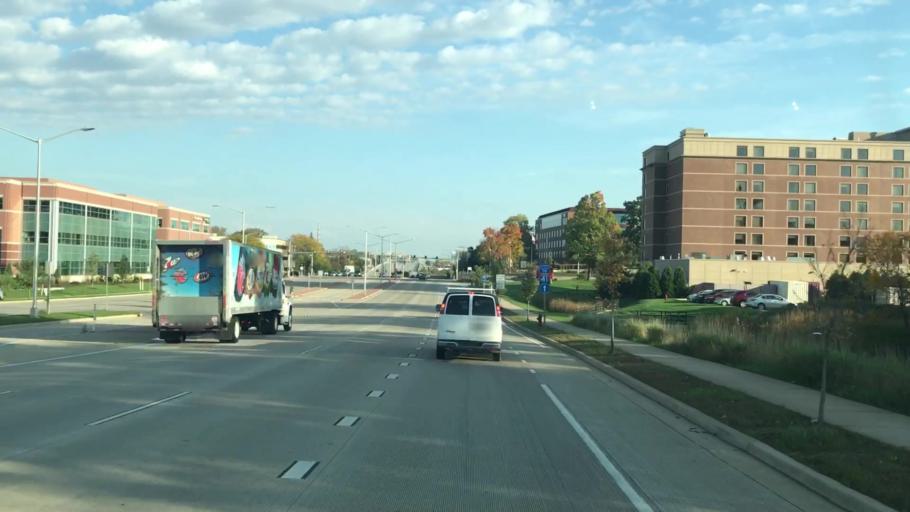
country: US
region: Wisconsin
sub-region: Waukesha County
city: Elm Grove
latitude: 43.0435
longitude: -88.0470
